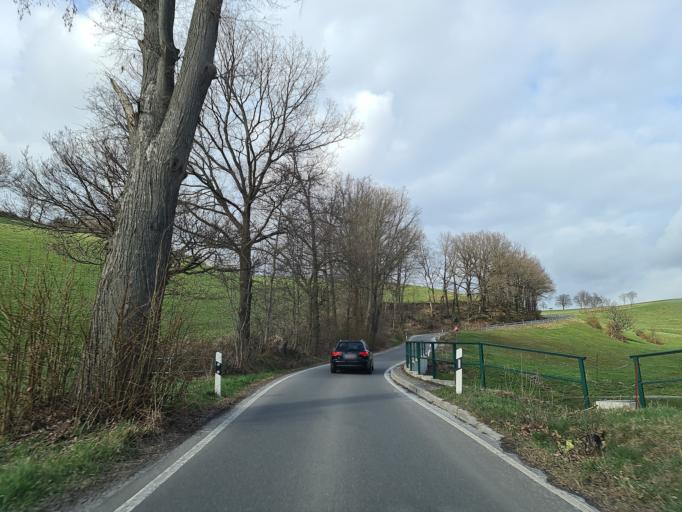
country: DE
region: Saxony
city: Reinsdorf
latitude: 50.7157
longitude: 12.6188
